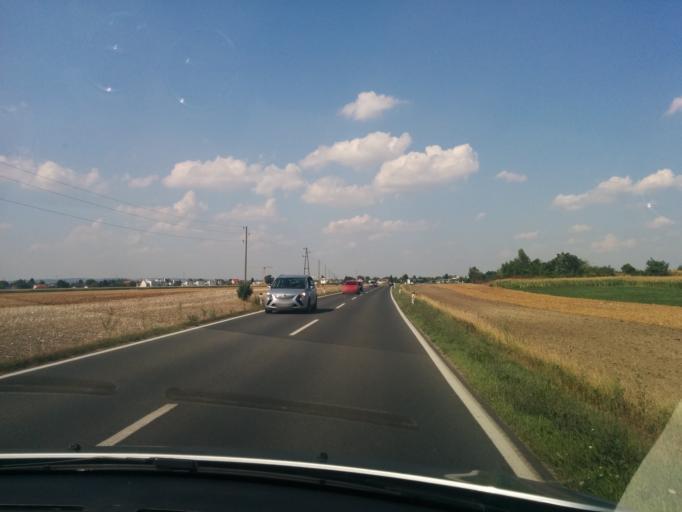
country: AT
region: Lower Austria
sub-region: Politischer Bezirk Wien-Umgebung
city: Gerasdorf bei Wien
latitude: 48.2850
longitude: 16.4617
